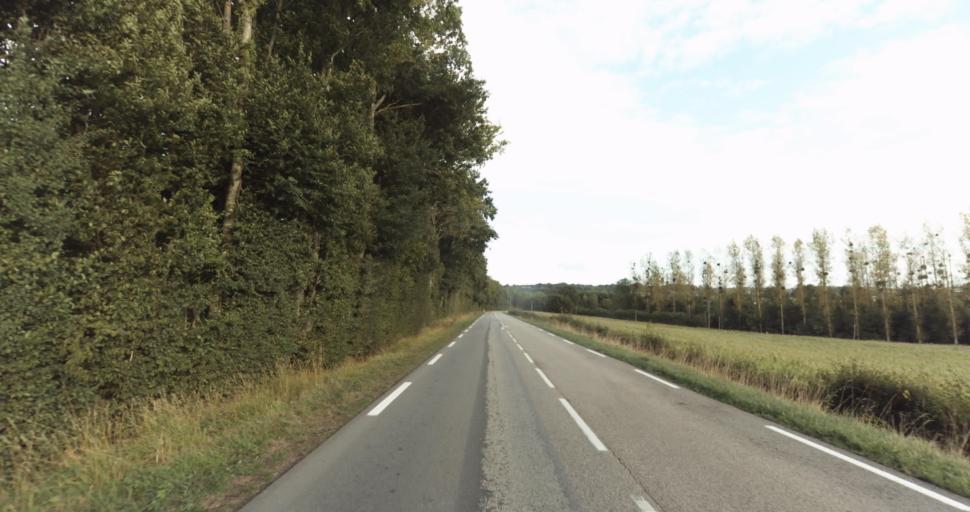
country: FR
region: Lower Normandy
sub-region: Departement de l'Orne
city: Sainte-Gauburge-Sainte-Colombe
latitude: 48.7225
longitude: 0.4225
